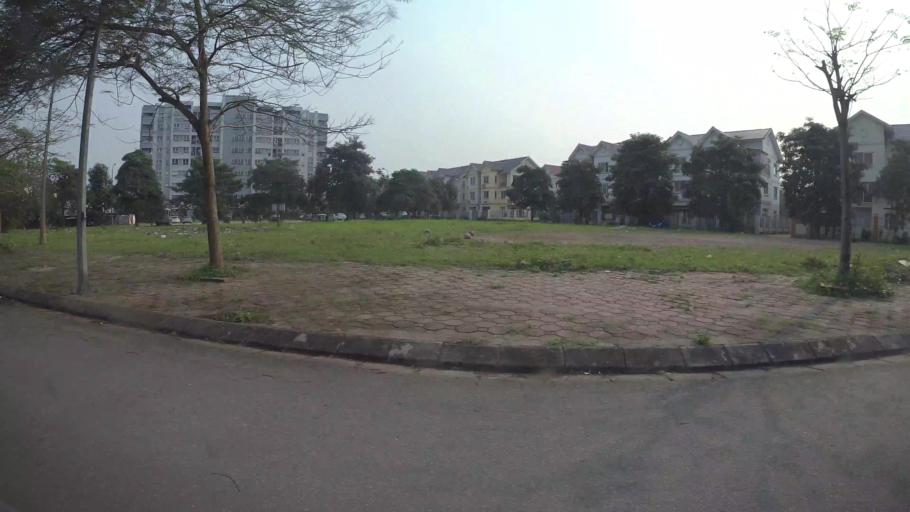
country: VN
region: Ha Noi
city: Ha Dong
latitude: 20.9982
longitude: 105.7473
